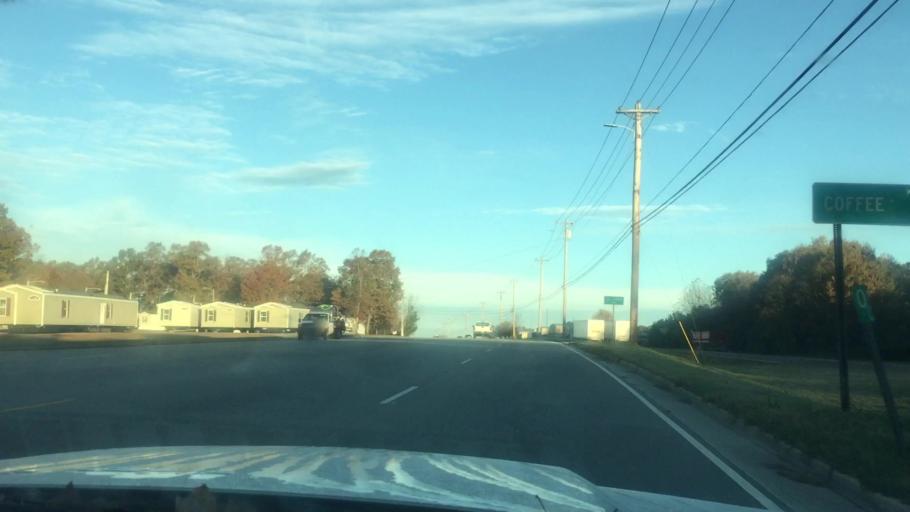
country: US
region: Tennessee
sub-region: Coffee County
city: Tullahoma
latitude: 35.3446
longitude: -86.1941
